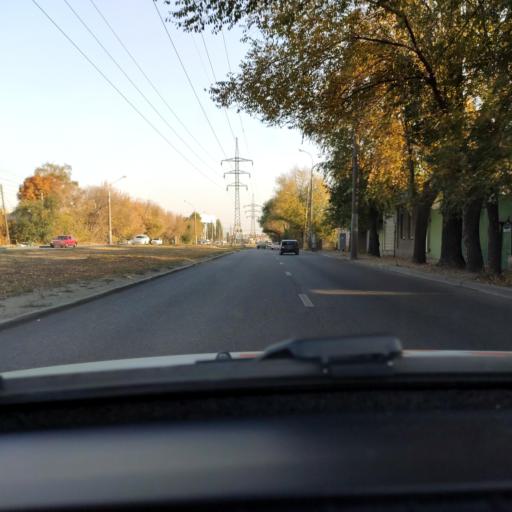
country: RU
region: Voronezj
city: Voronezh
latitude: 51.6372
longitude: 39.1674
